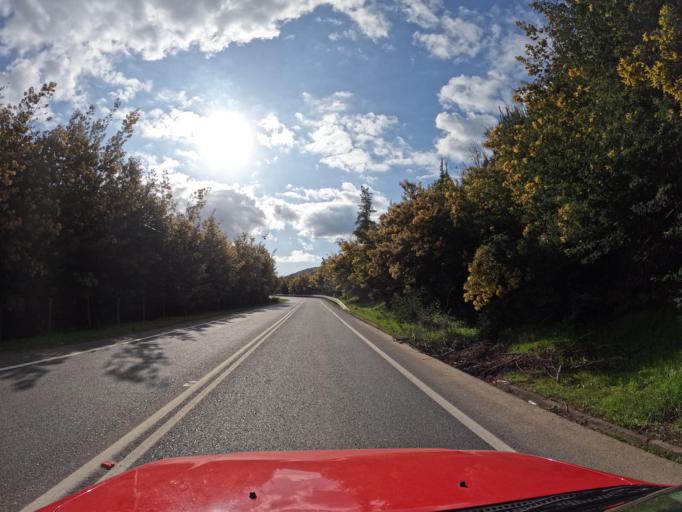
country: CL
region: Maule
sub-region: Provincia de Talca
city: Constitucion
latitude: -35.5430
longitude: -72.1527
